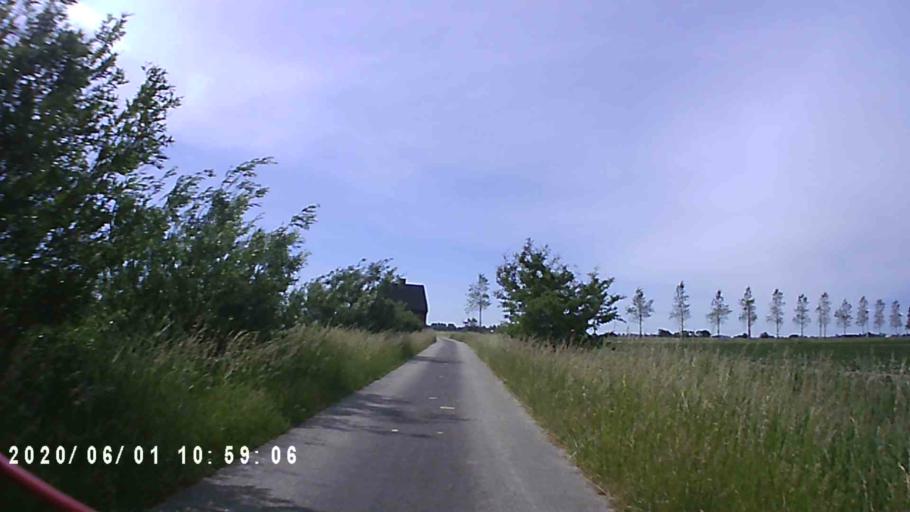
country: NL
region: Friesland
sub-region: Gemeente Franekeradeel
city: Sexbierum
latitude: 53.1993
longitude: 5.4927
